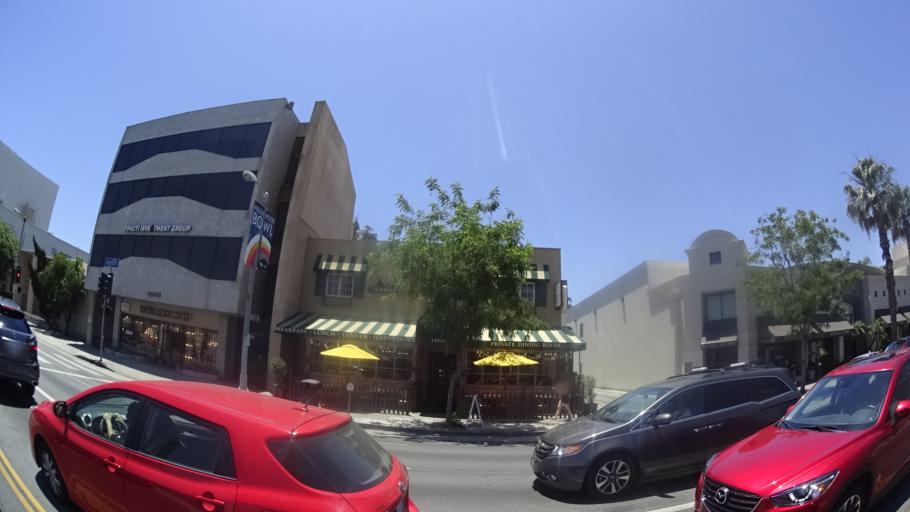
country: US
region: California
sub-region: Los Angeles County
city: Sherman Oaks
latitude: 34.1525
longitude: -118.4577
